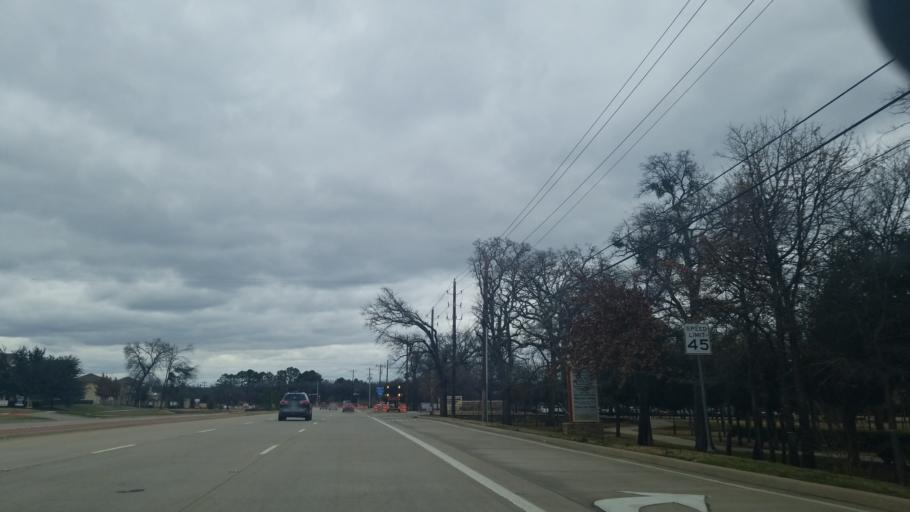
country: US
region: Texas
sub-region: Denton County
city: Flower Mound
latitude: 33.0445
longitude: -97.0693
